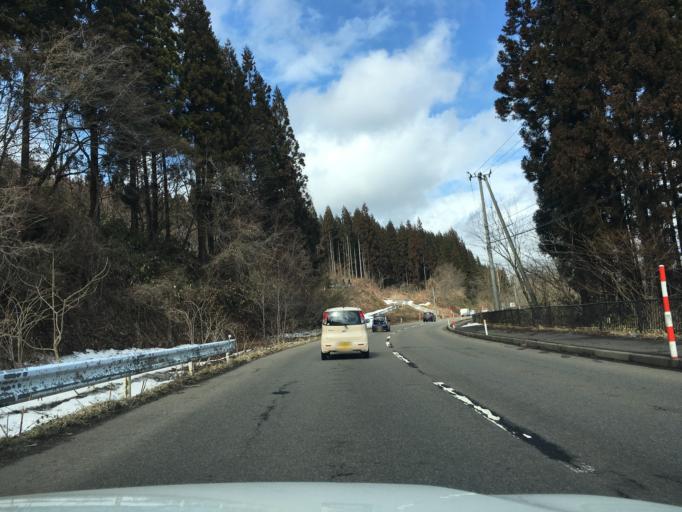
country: JP
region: Akita
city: Takanosu
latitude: 40.0156
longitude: 140.2763
